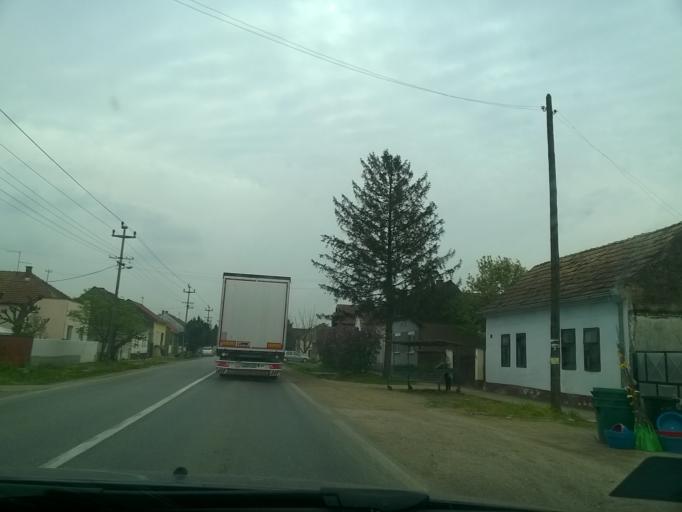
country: RS
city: Hrtkovci
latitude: 44.8810
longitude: 19.7637
